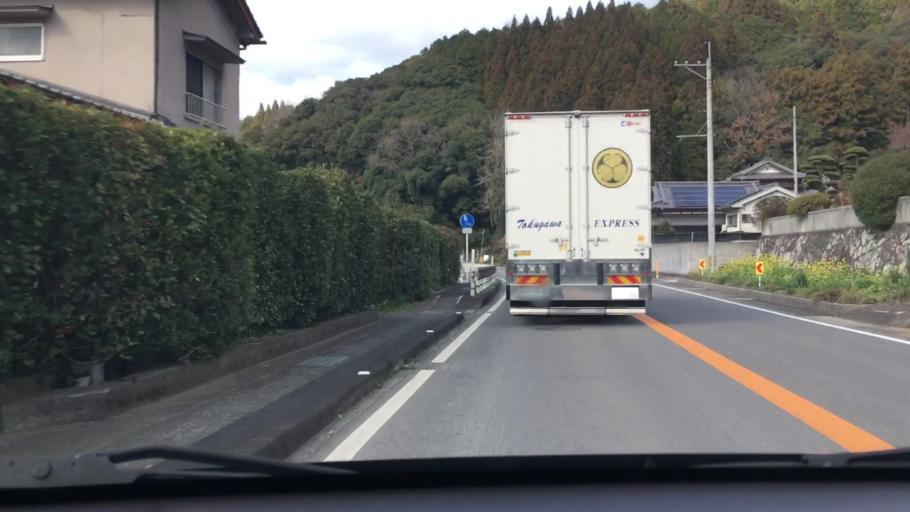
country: JP
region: Oita
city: Usuki
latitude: 33.0088
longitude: 131.7078
